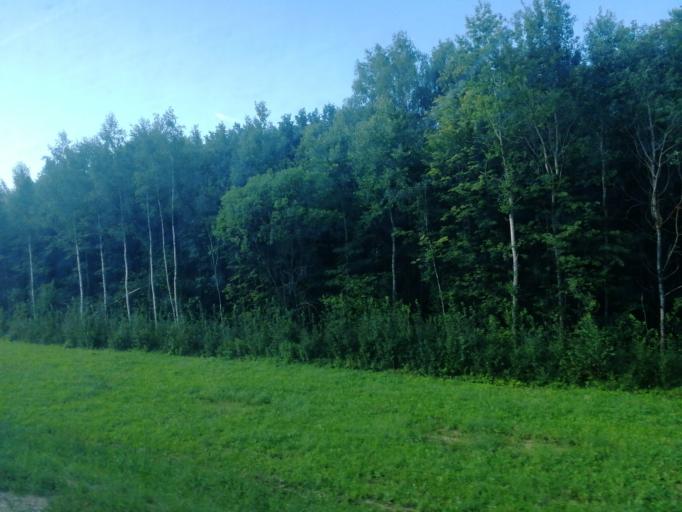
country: RU
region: Tula
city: Leninskiy
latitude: 54.2360
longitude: 37.3518
